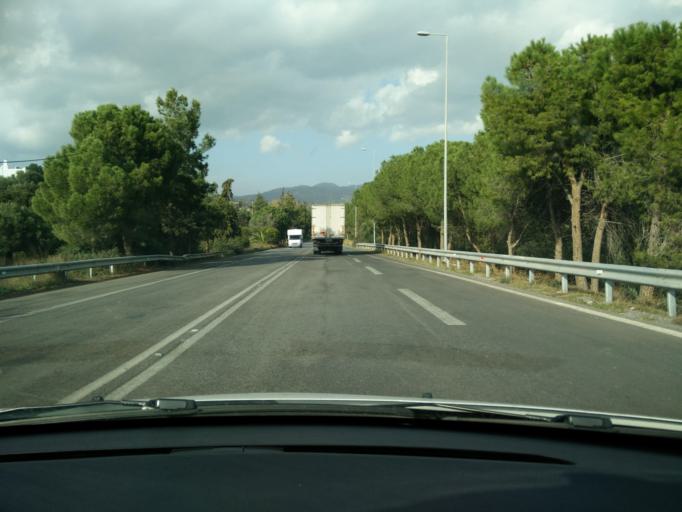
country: GR
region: Crete
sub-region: Nomos Lasithiou
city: Agios Nikolaos
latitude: 35.1889
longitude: 25.7037
